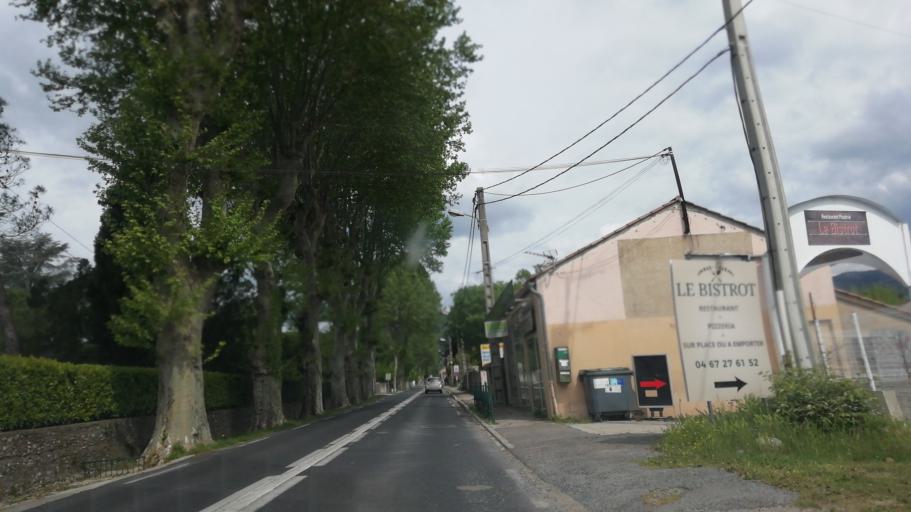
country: FR
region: Languedoc-Roussillon
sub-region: Departement de l'Herault
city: Ganges
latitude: 43.9275
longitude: 3.7149
